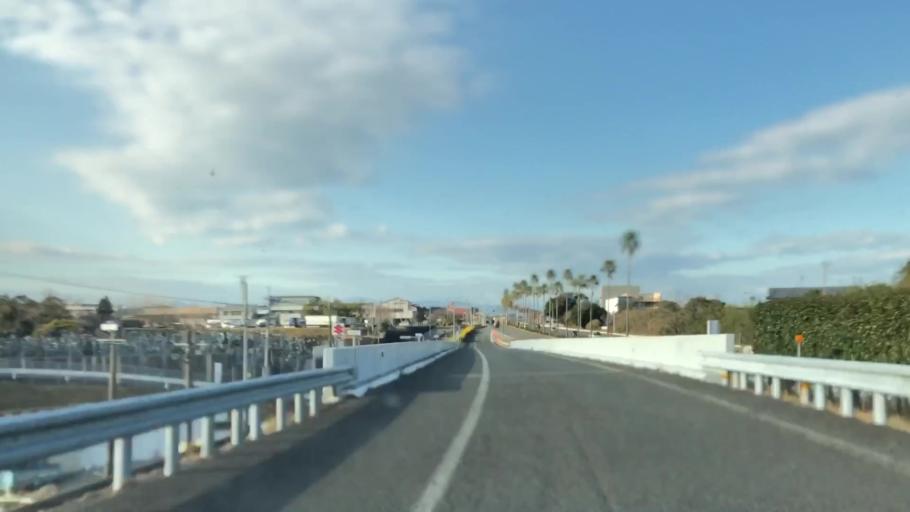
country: JP
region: Miyazaki
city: Miyazaki-shi
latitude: 31.8715
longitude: 131.4144
